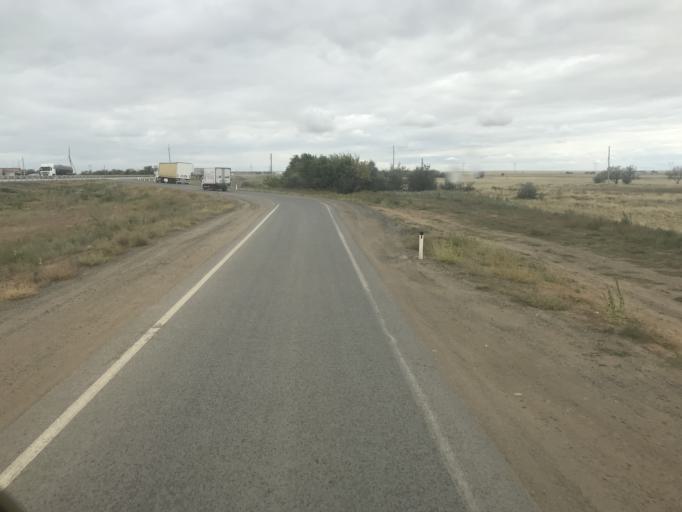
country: KZ
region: Pavlodar
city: Qalqaman
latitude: 51.9498
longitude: 75.9844
